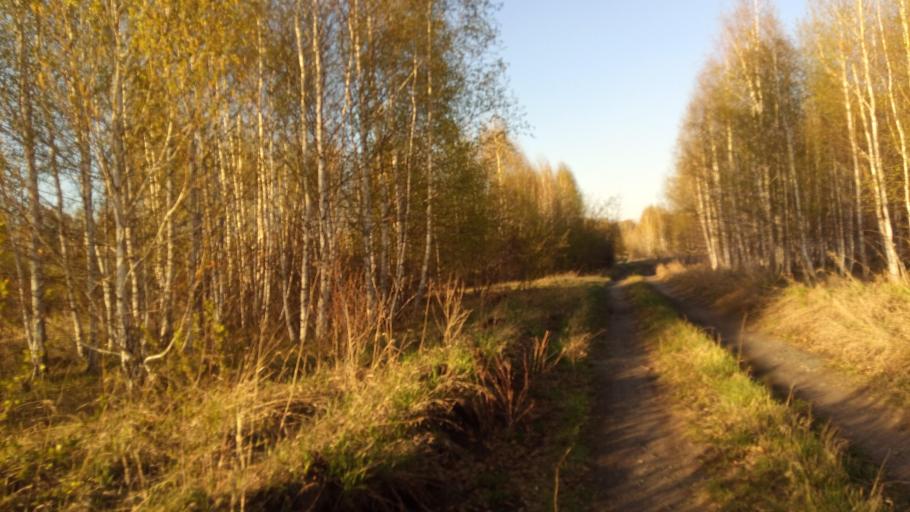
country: RU
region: Chelyabinsk
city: Timiryazevskiy
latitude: 54.9898
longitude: 60.8589
